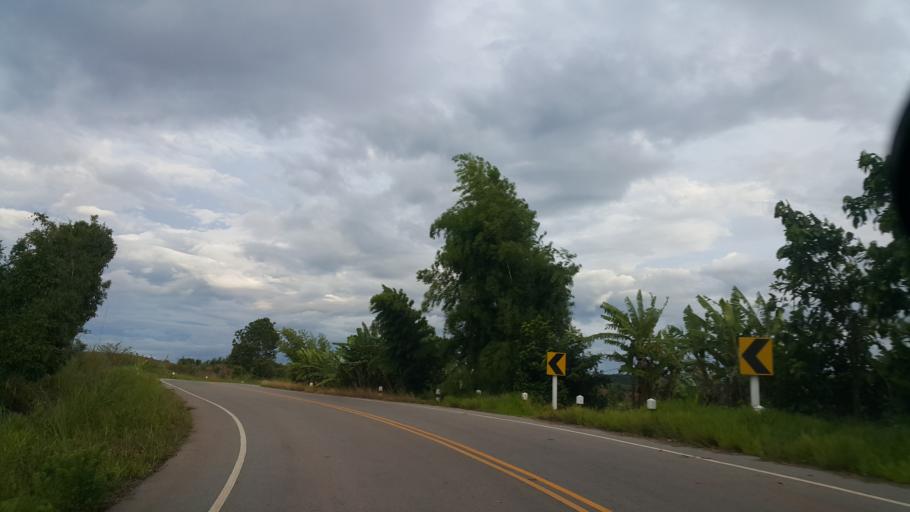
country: TH
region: Loei
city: Na Haeo
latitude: 17.4713
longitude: 101.1154
